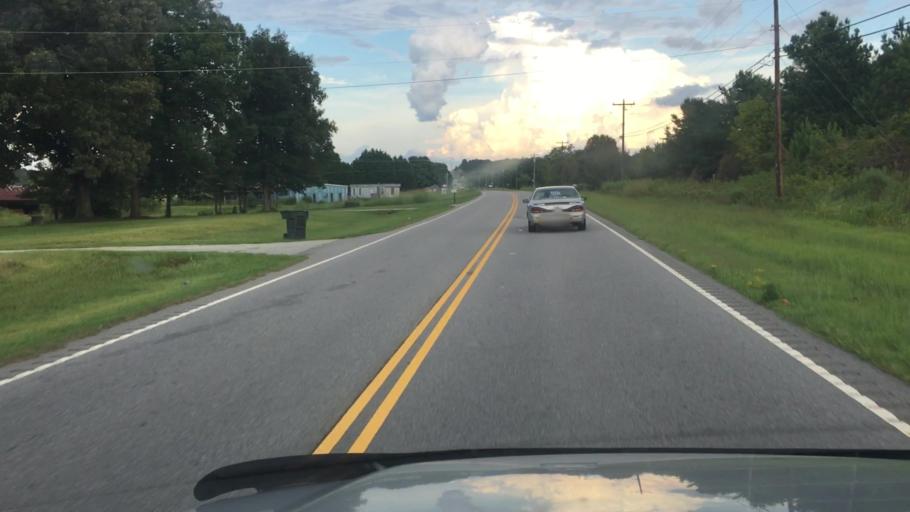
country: US
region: South Carolina
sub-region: Spartanburg County
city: Mayo
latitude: 35.1304
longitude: -81.7946
